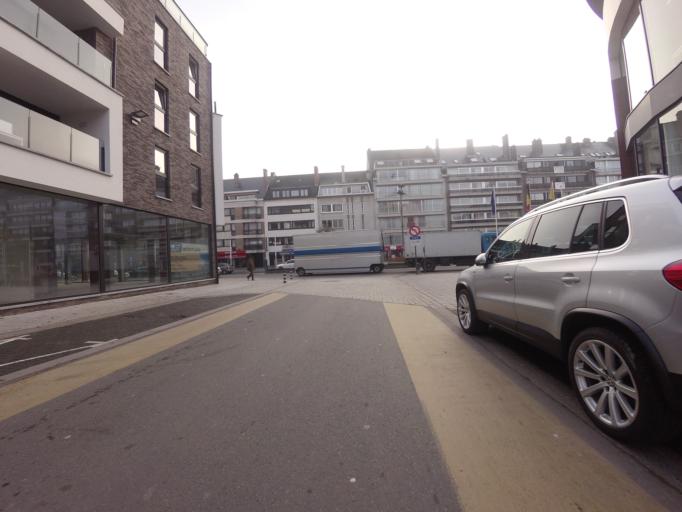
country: BE
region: Flanders
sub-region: Provincie Oost-Vlaanderen
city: Ninove
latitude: 50.8347
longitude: 4.0210
